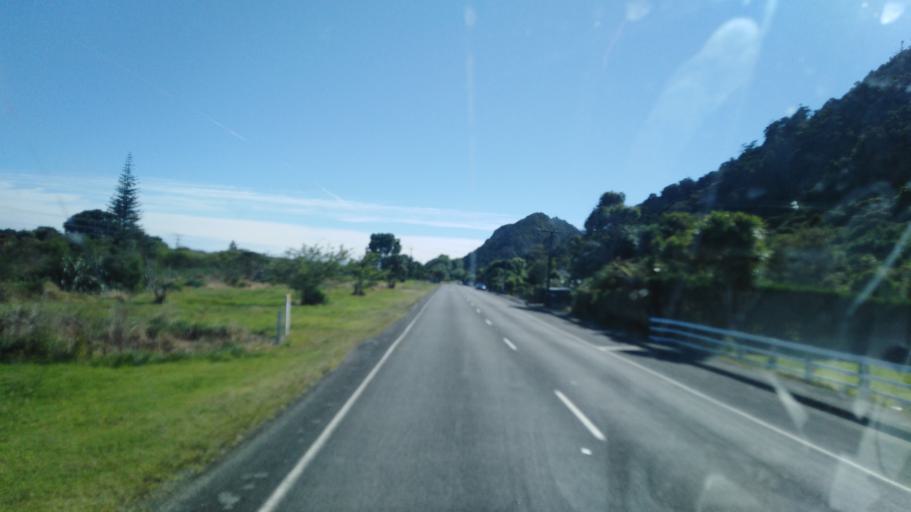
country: NZ
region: West Coast
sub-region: Buller District
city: Westport
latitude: -41.6345
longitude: 171.8501
